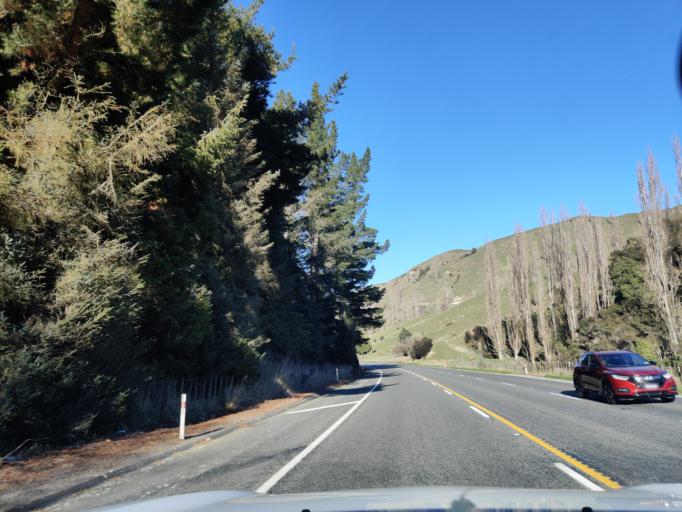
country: NZ
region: Manawatu-Wanganui
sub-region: Ruapehu District
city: Waiouru
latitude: -39.7754
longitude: 175.7899
